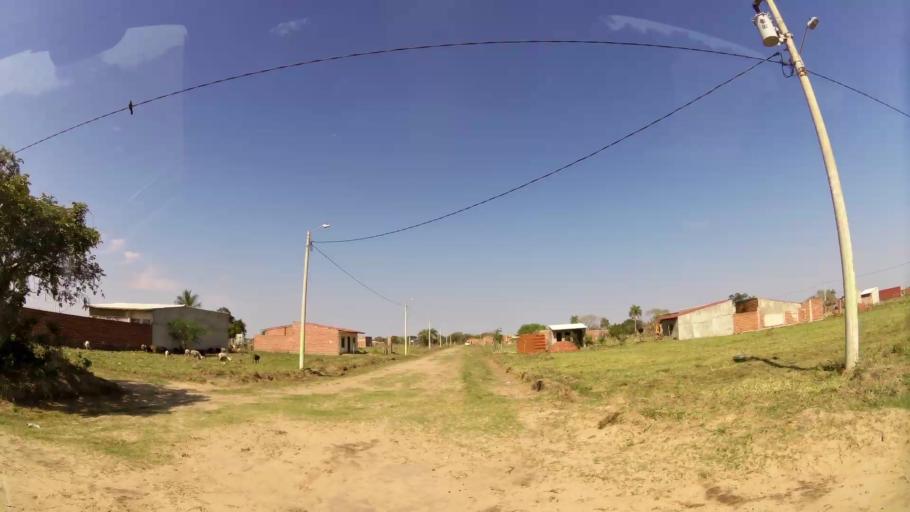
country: BO
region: Santa Cruz
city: Cotoca
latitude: -17.7192
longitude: -63.0666
